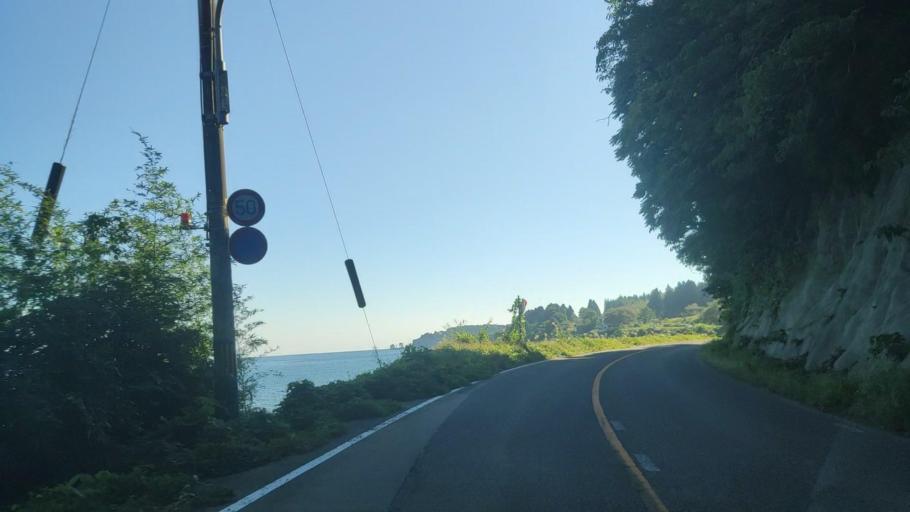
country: JP
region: Ishikawa
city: Nanao
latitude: 37.2730
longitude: 137.0969
